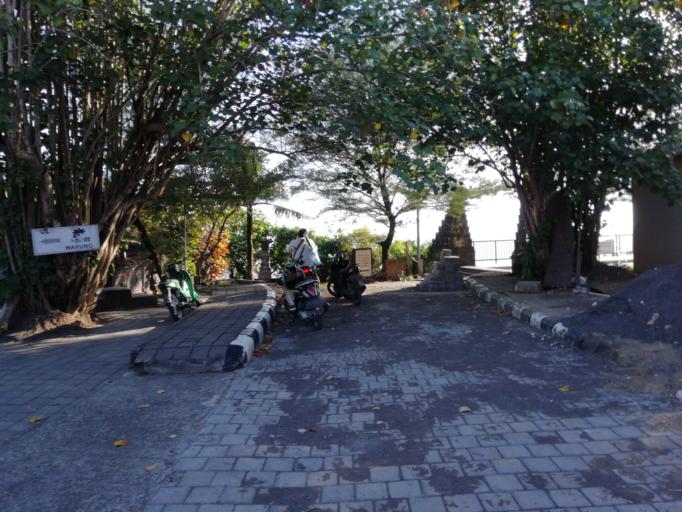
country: ID
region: Bali
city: Banjar Pangkungtibah Selatan
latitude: -8.6171
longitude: 115.0861
